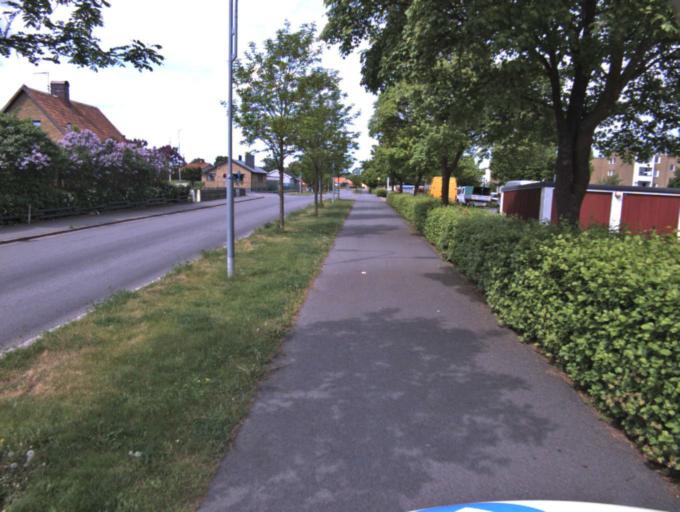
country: SE
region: Skane
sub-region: Kristianstads Kommun
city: Kristianstad
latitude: 56.0566
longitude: 14.1547
